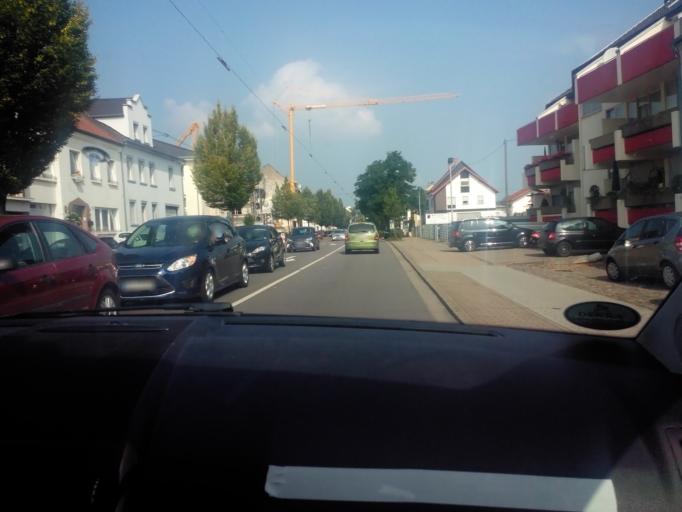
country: DE
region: Saarland
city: Saarlouis
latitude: 49.3060
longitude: 6.7572
